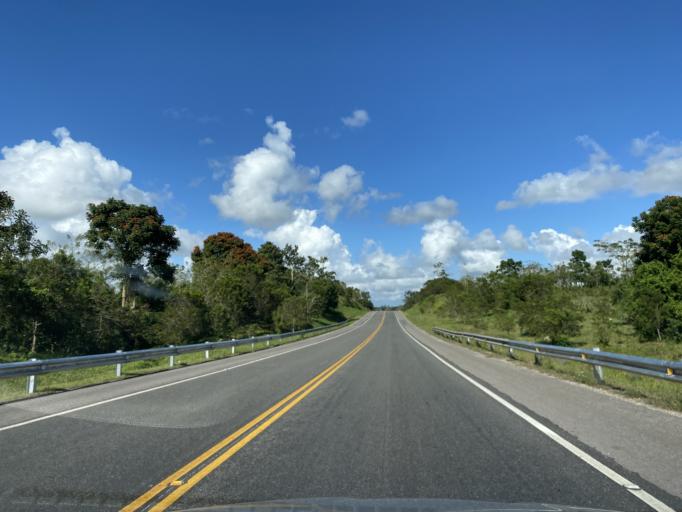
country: DO
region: Monte Plata
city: Majagual
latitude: 19.0156
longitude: -69.8229
